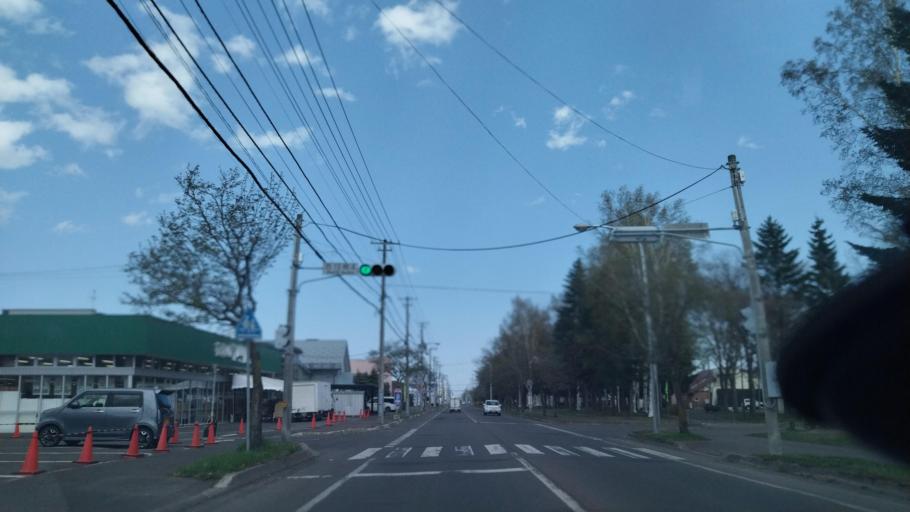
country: JP
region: Hokkaido
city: Obihiro
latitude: 42.9085
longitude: 143.1554
